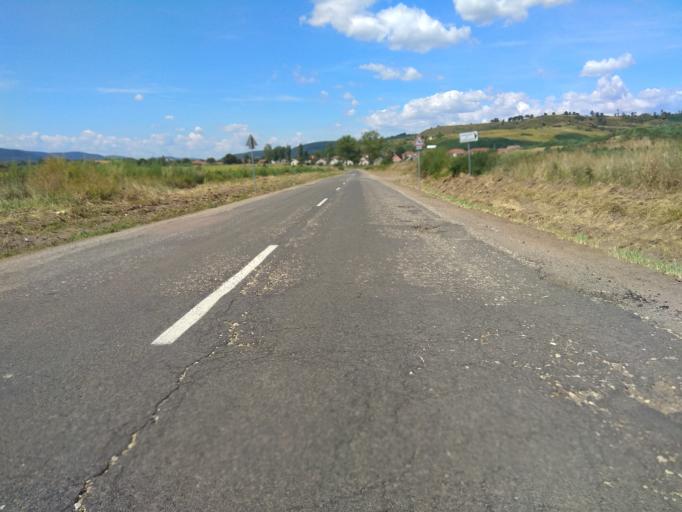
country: HU
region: Borsod-Abauj-Zemplen
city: Sajokaza
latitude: 48.2877
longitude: 20.6062
